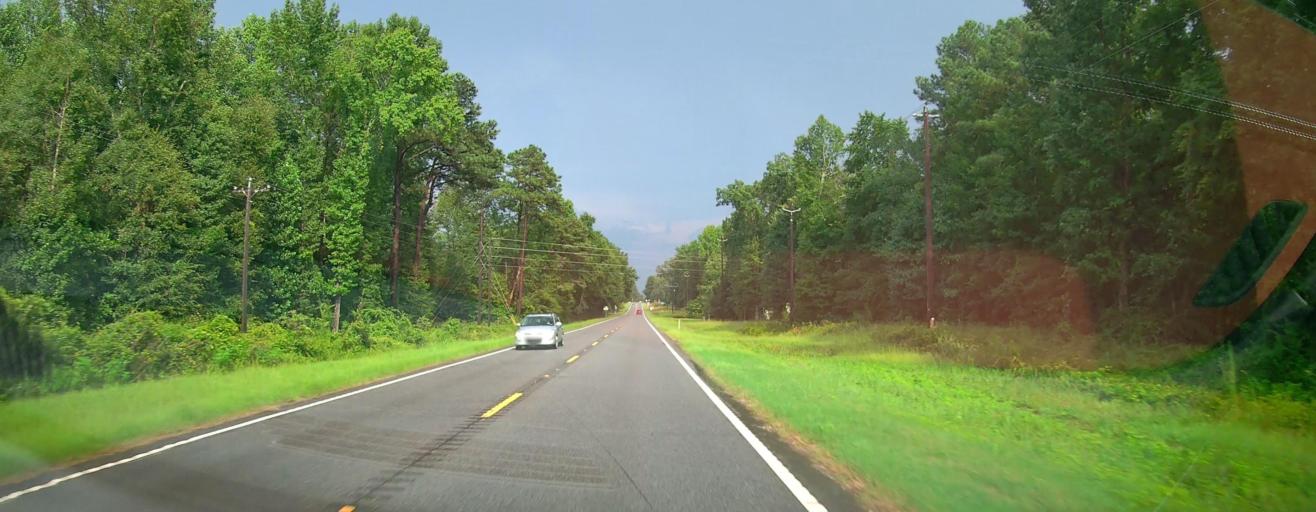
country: US
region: Georgia
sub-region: Twiggs County
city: Jeffersonville
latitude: 32.6062
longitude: -83.2586
